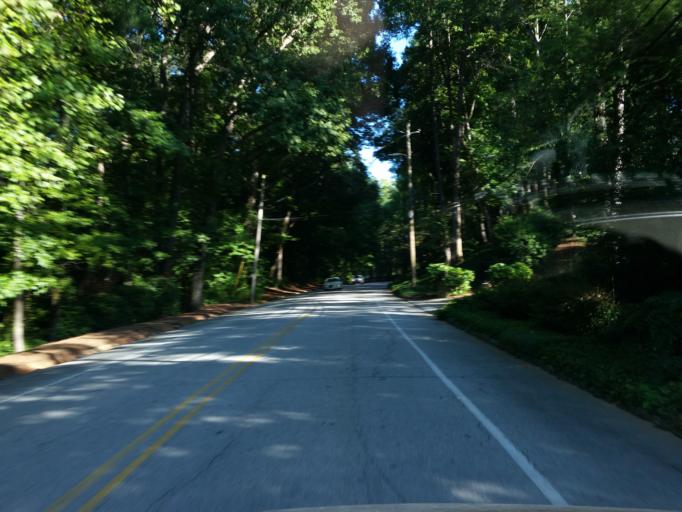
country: US
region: Georgia
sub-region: Cobb County
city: Vinings
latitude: 33.8561
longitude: -84.4414
